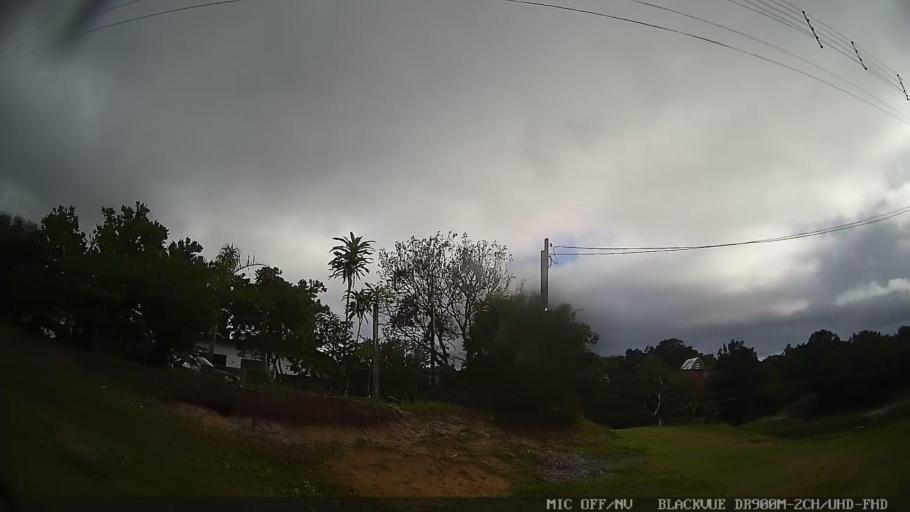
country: BR
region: Sao Paulo
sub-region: Peruibe
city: Peruibe
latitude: -24.2478
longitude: -46.9020
